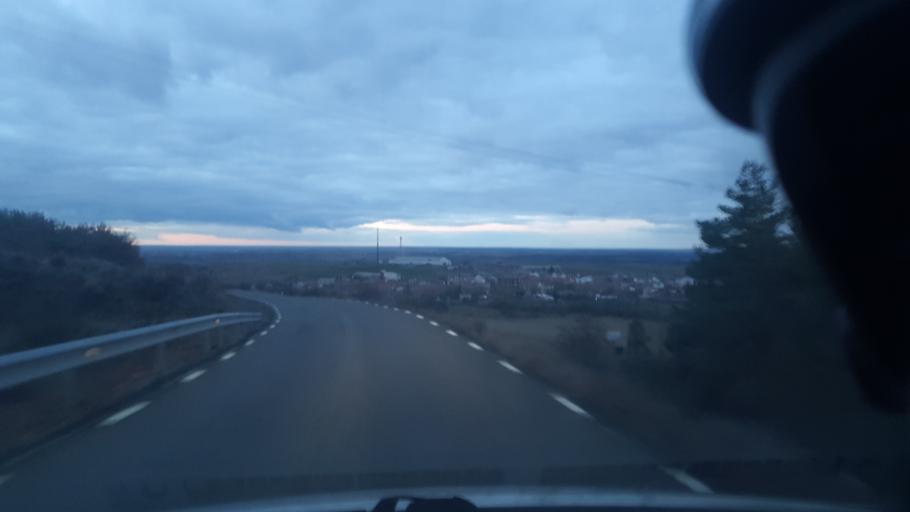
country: ES
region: Castille and Leon
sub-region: Provincia de Avila
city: Ojos-Albos
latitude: 40.7374
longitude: -4.4703
